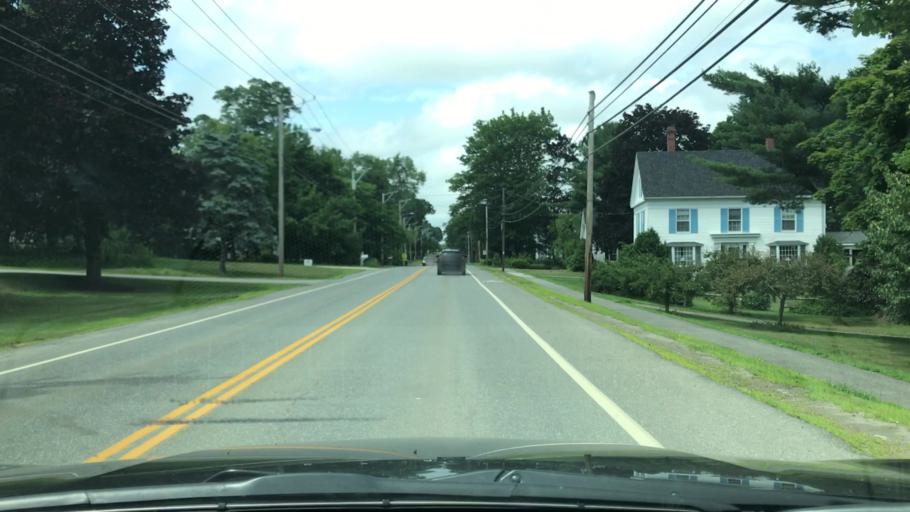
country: US
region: Maine
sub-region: Waldo County
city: Belfast
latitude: 44.4150
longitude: -68.9964
